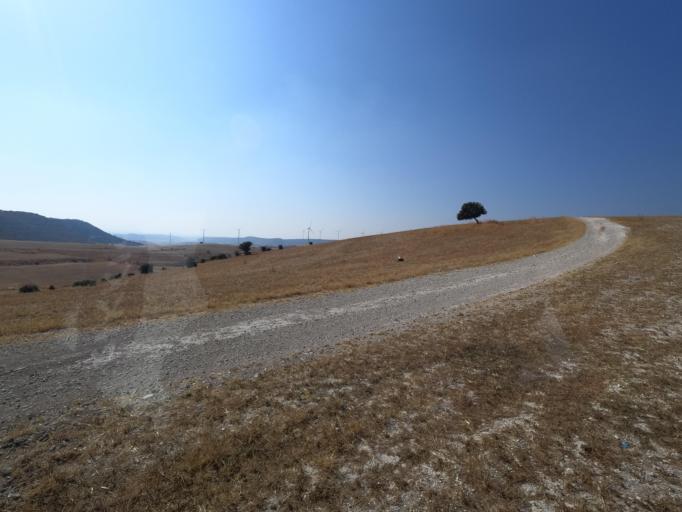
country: CY
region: Lefkosia
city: Lympia
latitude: 34.9814
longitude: 33.4848
